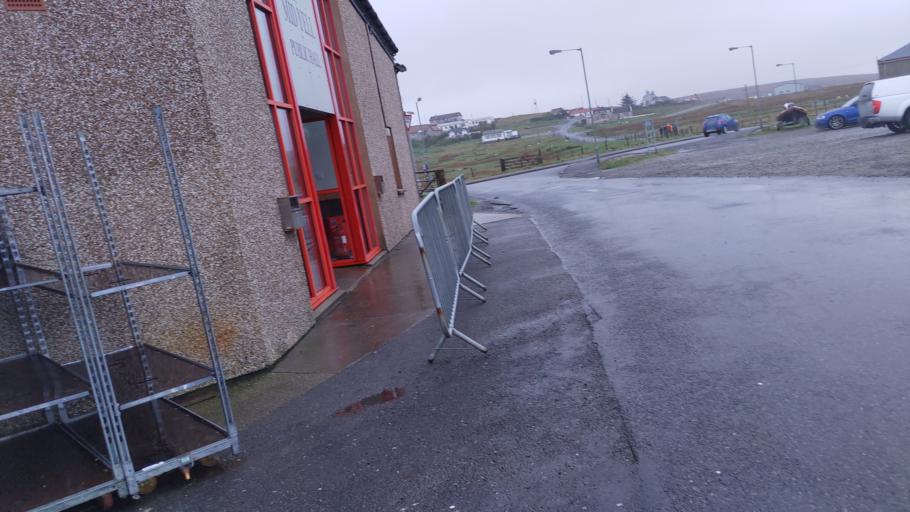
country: GB
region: Scotland
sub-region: Shetland Islands
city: Shetland
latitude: 60.5997
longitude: -1.0681
